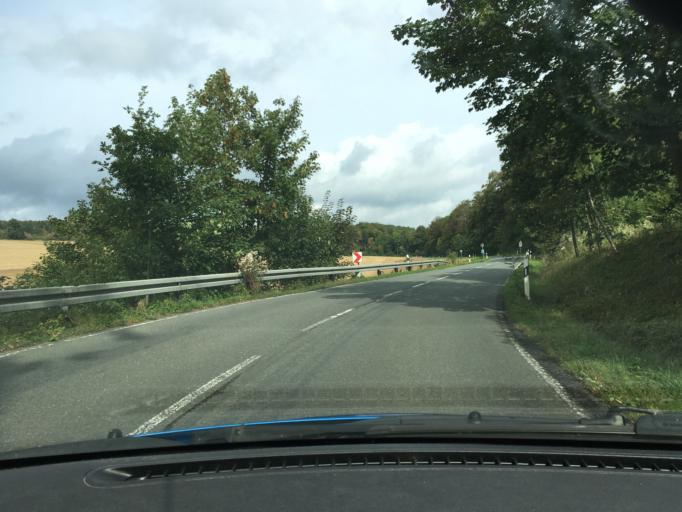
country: DE
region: Lower Saxony
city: Messenkamp
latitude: 52.2410
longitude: 9.4280
